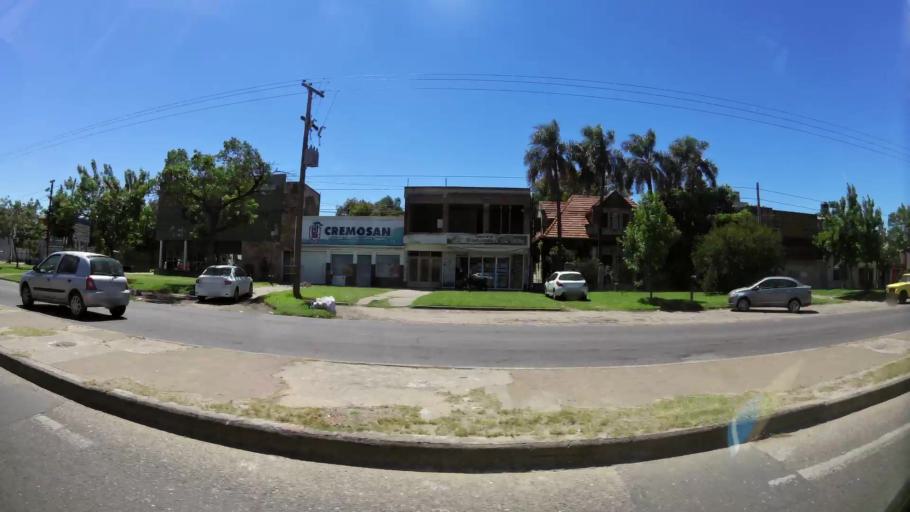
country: AR
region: Santa Fe
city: Santa Fe de la Vera Cruz
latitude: -31.6193
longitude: -60.7134
